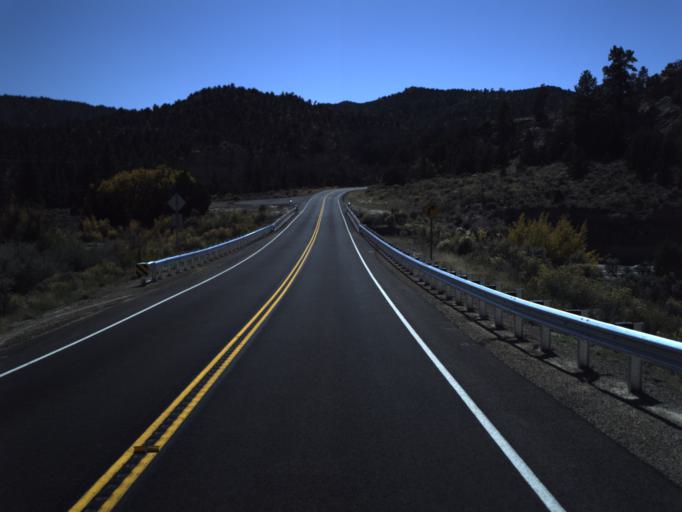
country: US
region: Utah
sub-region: Garfield County
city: Panguitch
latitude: 37.6145
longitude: -111.8958
